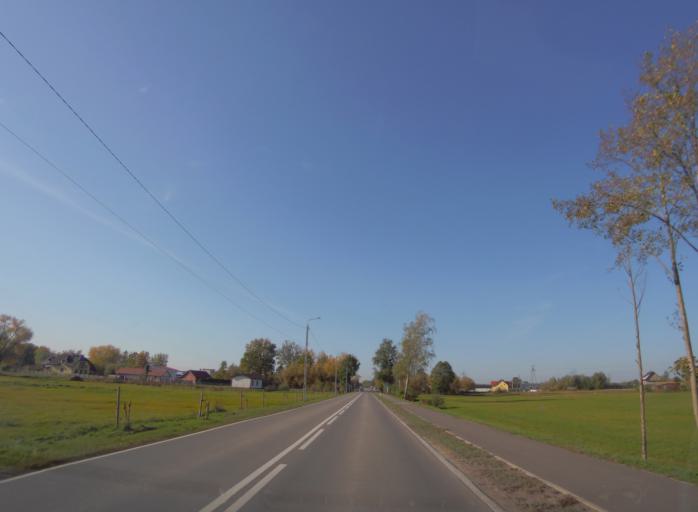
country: PL
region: Masovian Voivodeship
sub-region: Powiat minski
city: Halinow
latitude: 52.1886
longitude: 21.3183
